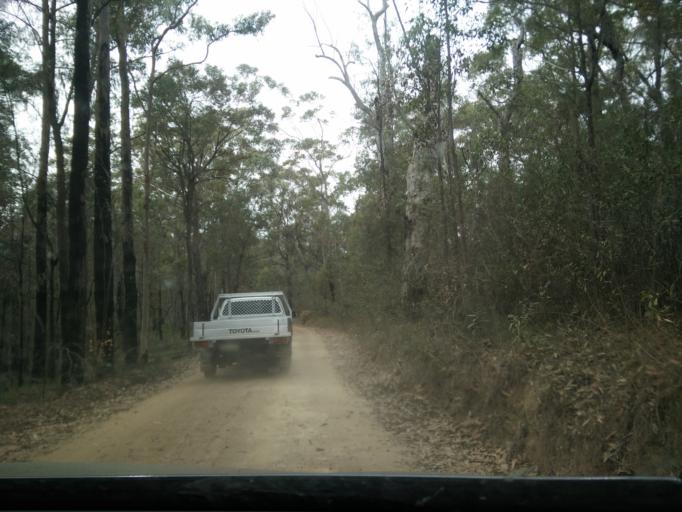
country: AU
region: New South Wales
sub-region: Blue Mountains Municipality
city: Glenbrook
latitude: -33.8145
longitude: 150.5647
